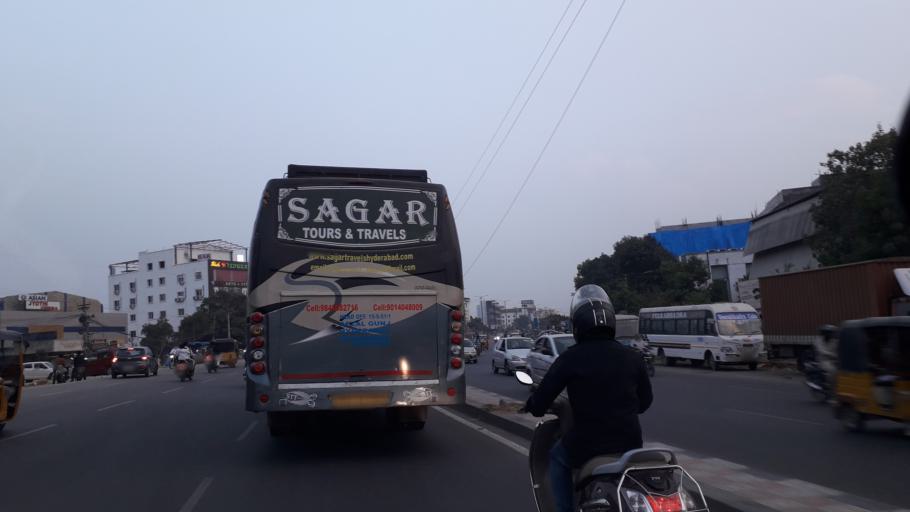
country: IN
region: Telangana
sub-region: Medak
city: Serilingampalle
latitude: 17.5032
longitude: 78.3109
